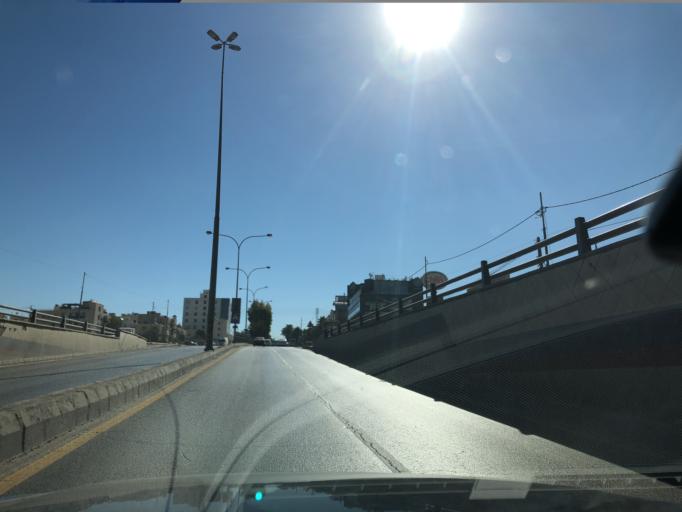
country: JO
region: Amman
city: Al Jubayhah
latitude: 31.9743
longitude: 35.8667
